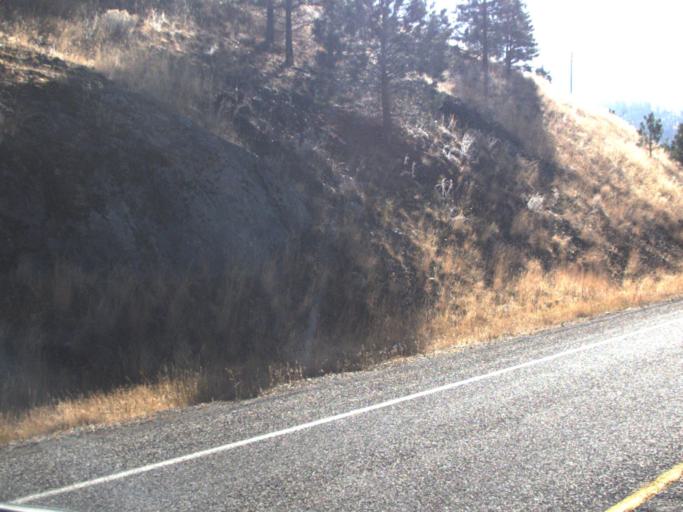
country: US
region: Washington
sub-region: Ferry County
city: Republic
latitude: 48.6644
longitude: -118.6663
